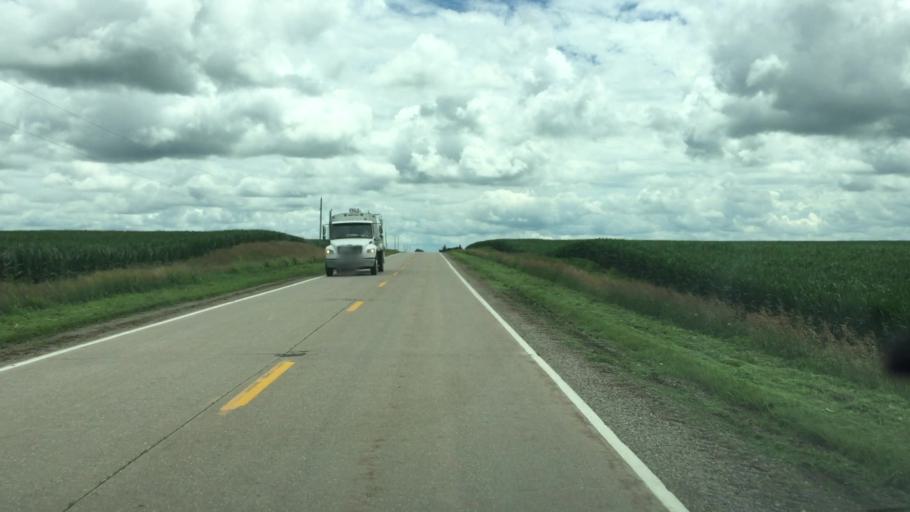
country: US
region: Iowa
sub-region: Jasper County
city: Monroe
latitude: 41.5807
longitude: -93.1352
